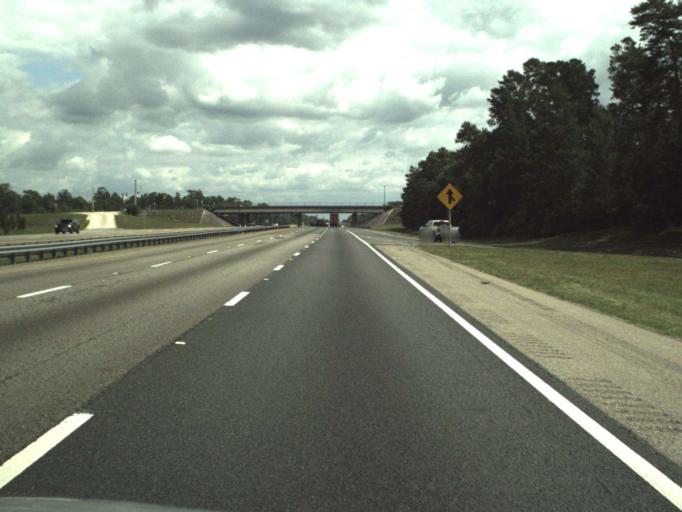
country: US
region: Florida
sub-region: Volusia County
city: Lake Helen
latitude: 28.9521
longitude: -81.2585
